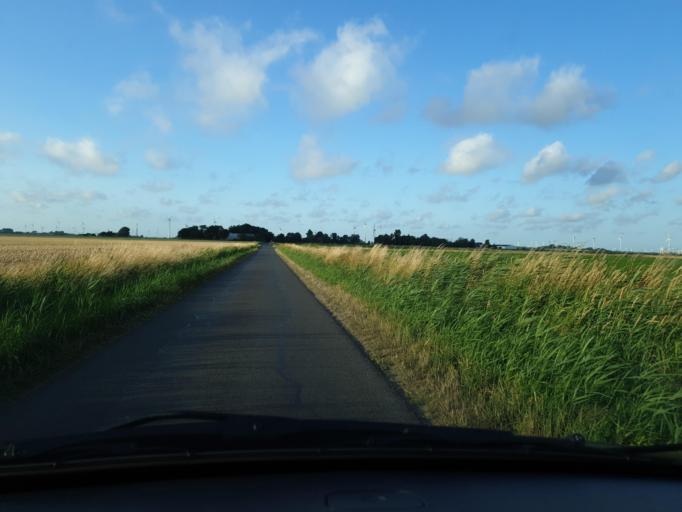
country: DE
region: Schleswig-Holstein
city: Busumer Deichhausen
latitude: 54.1413
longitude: 8.9120
